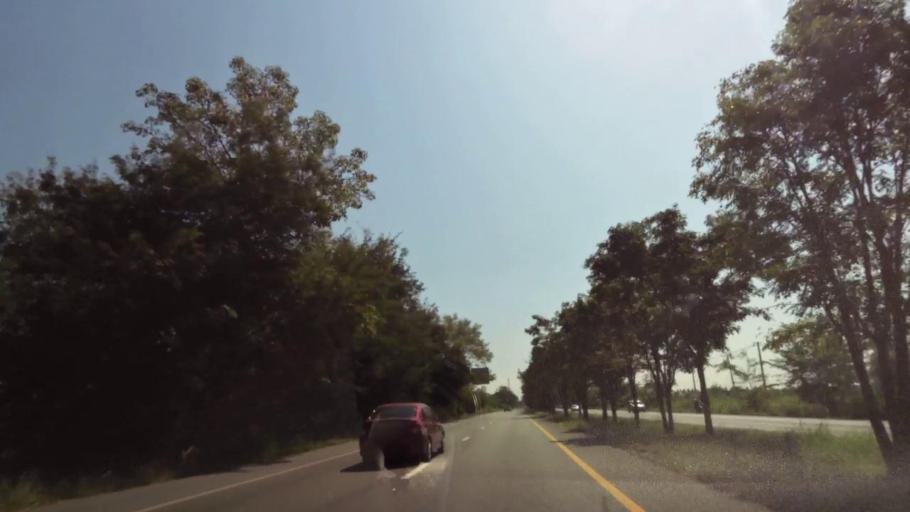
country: TH
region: Nakhon Sawan
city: Kao Liao
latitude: 15.8814
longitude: 100.1156
